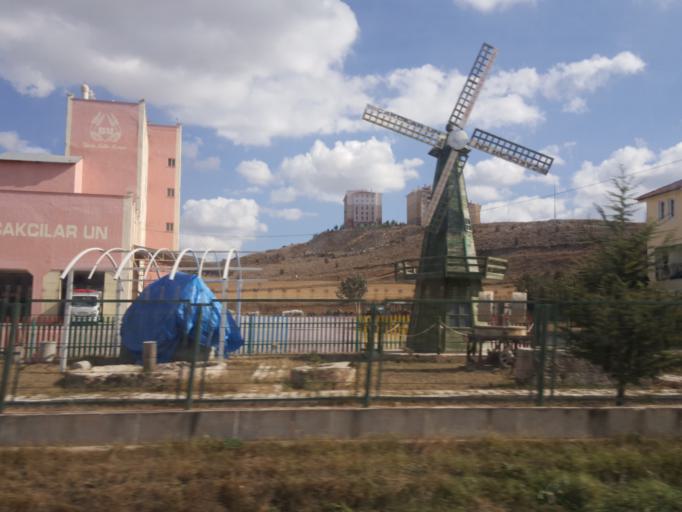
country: TR
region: Tokat
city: Artova
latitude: 40.1171
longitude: 36.3123
